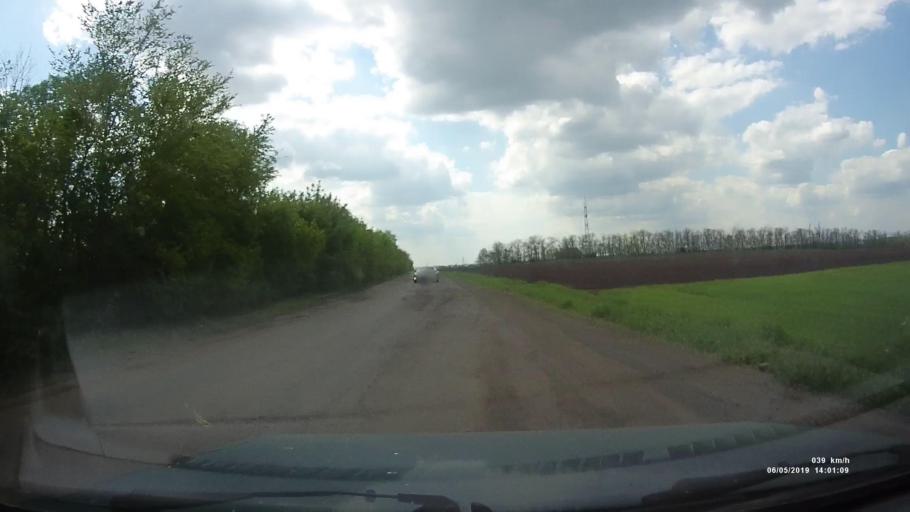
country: RU
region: Rostov
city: Shakhty
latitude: 47.6851
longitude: 40.3809
